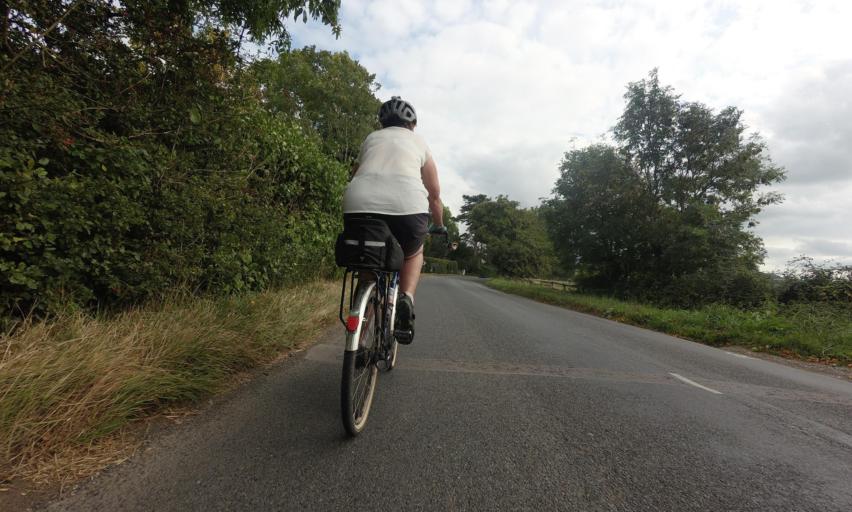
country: GB
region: England
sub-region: Gloucestershire
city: Winchcombe
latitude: 51.9862
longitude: -1.9987
